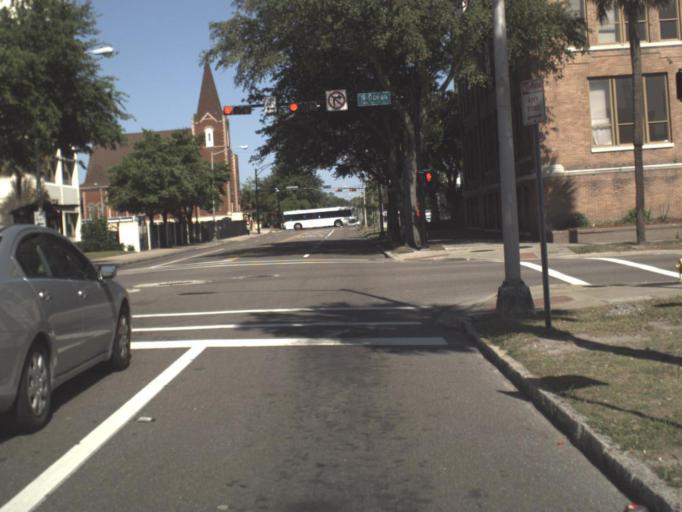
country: US
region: Florida
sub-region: Duval County
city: Jacksonville
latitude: 30.3313
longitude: -81.6555
